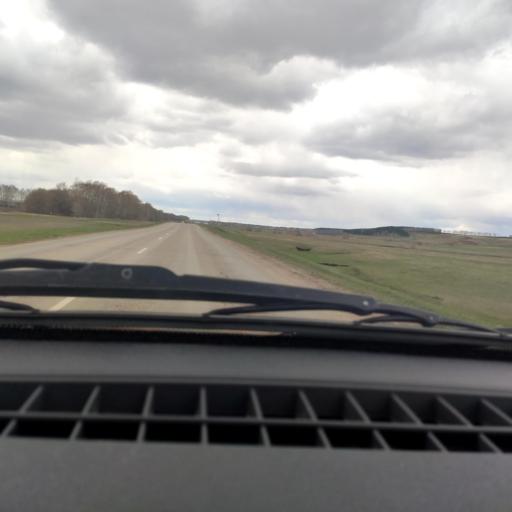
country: RU
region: Bashkortostan
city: Chekmagush
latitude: 55.1232
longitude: 54.7228
